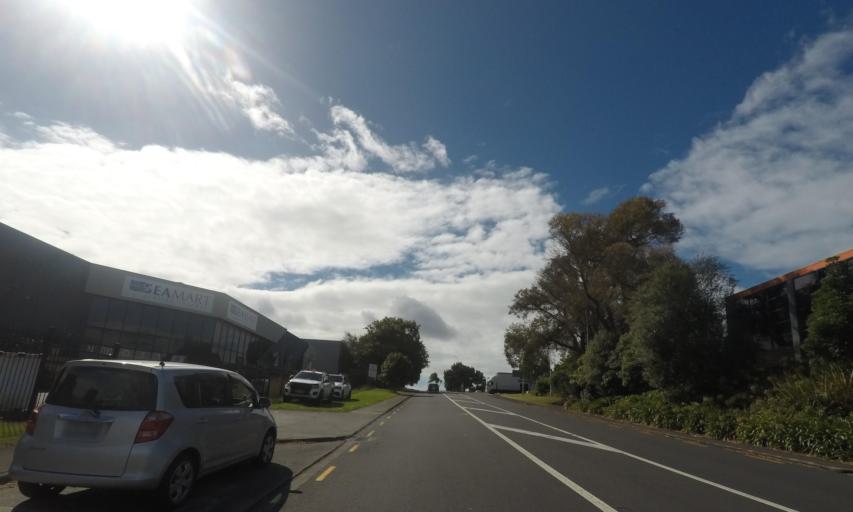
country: NZ
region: Auckland
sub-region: Auckland
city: Tamaki
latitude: -36.9248
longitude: 174.8522
